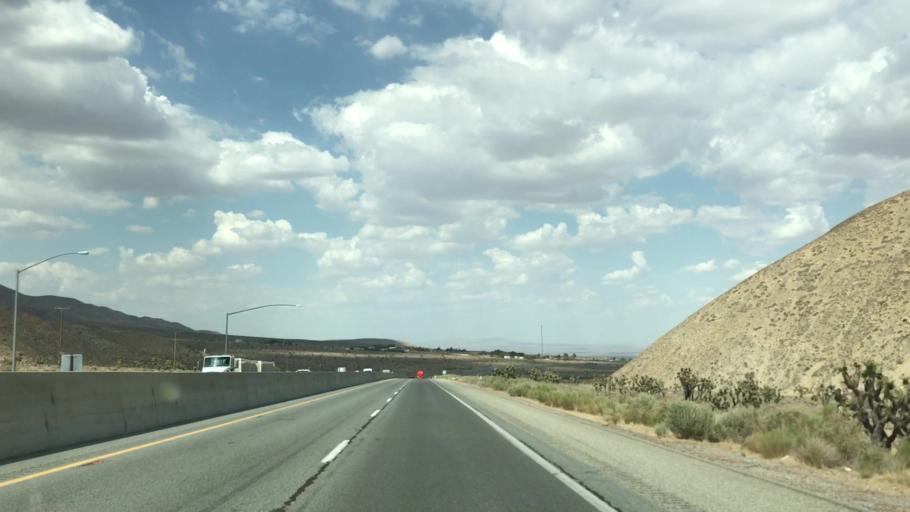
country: US
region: California
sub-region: Kern County
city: Mojave
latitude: 35.1144
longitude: -118.2330
